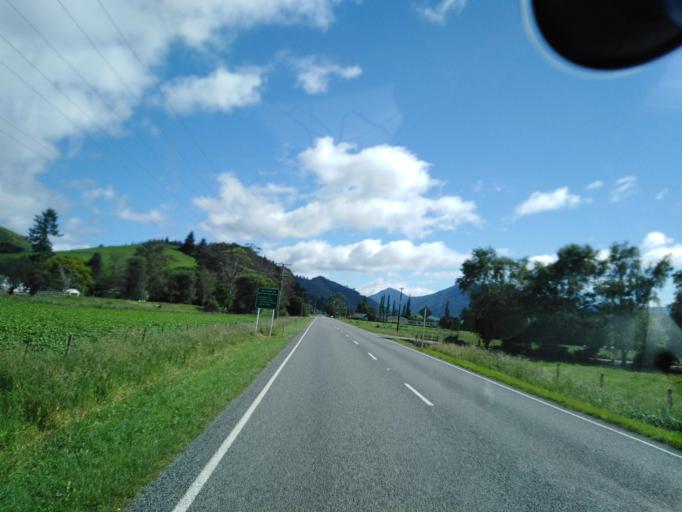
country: NZ
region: Nelson
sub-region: Nelson City
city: Nelson
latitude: -41.2381
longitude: 173.5798
